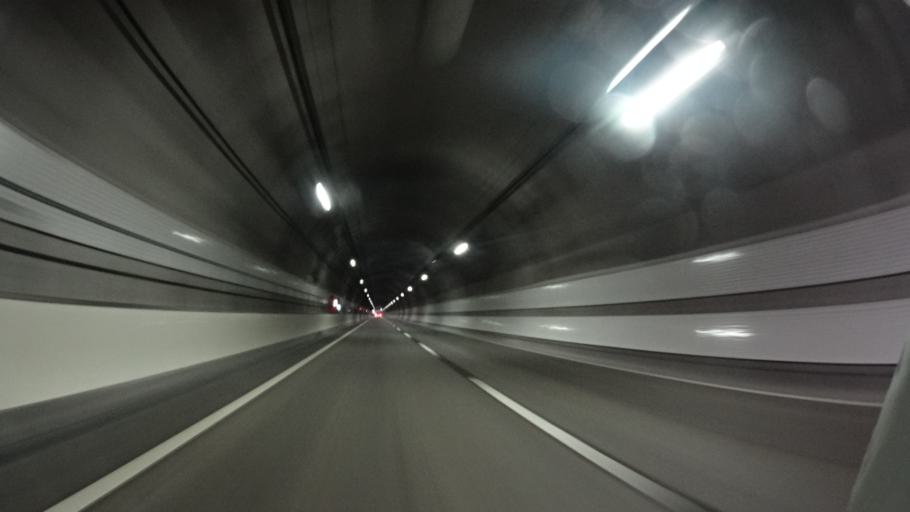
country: JP
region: Kyoto
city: Kyoto
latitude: 34.9727
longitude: 135.7744
